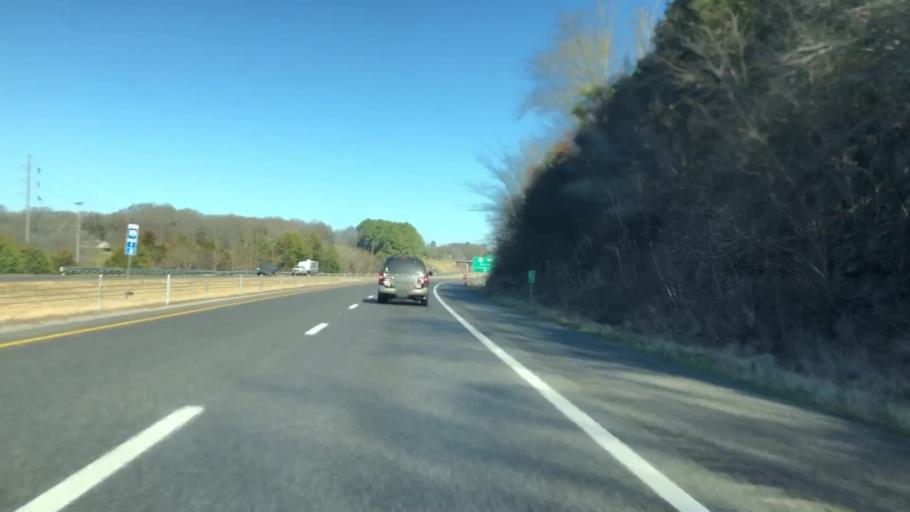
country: US
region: Alabama
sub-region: Limestone County
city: Ardmore
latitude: 35.0073
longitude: -86.8792
